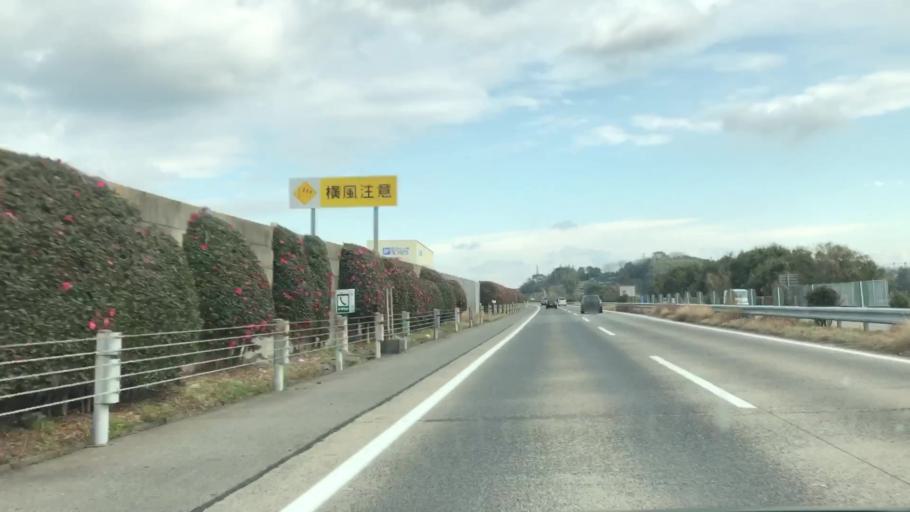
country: JP
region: Saga Prefecture
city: Kanzakimachi-kanzaki
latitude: 33.3542
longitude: 130.4058
